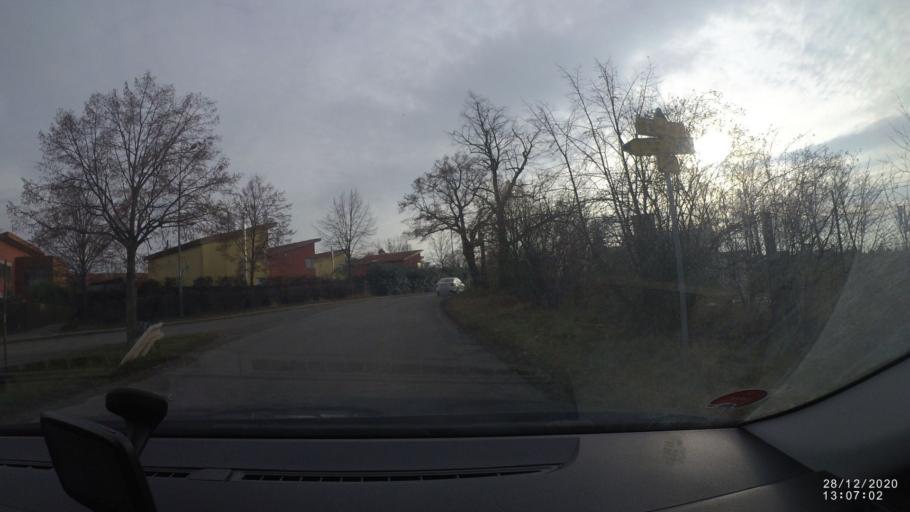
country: CZ
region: Central Bohemia
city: Zelenec
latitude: 50.1385
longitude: 14.6593
